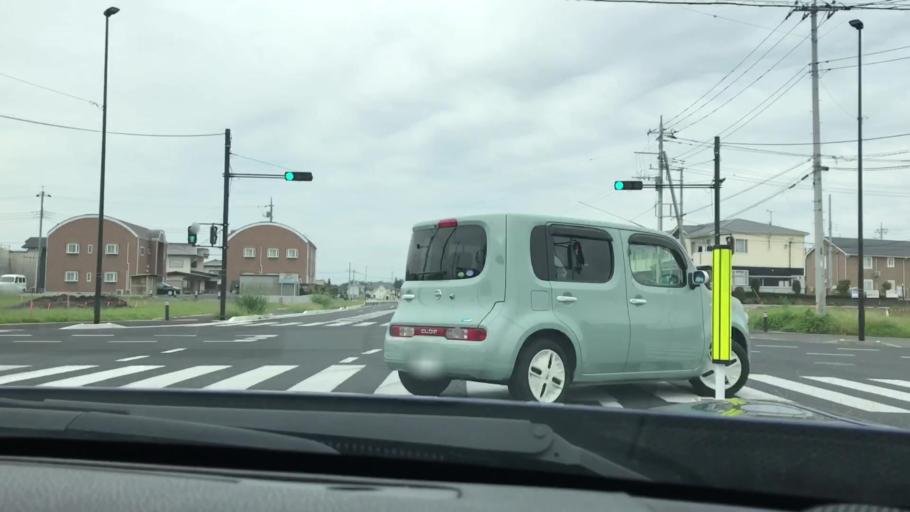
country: JP
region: Gunma
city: Kanekomachi
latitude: 36.3886
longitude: 139.0044
